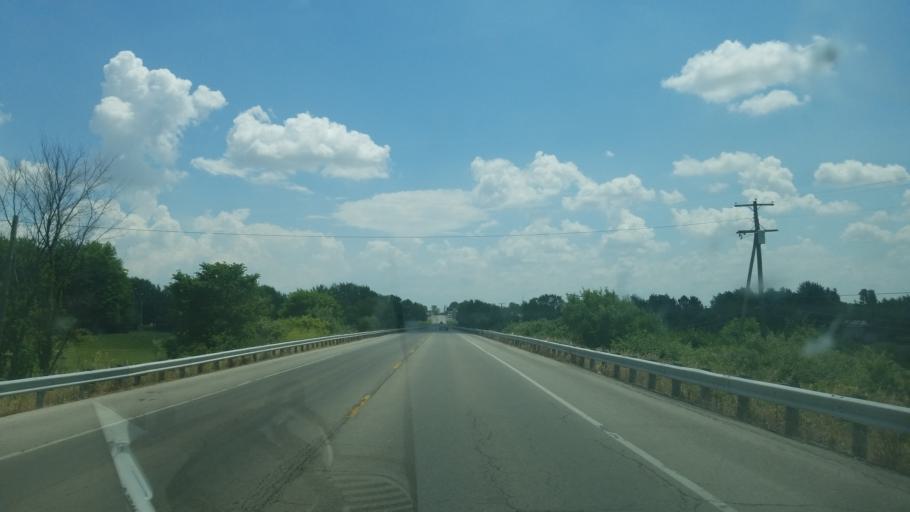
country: US
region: Ohio
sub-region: Hardin County
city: Kenton
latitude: 40.6548
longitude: -83.6318
